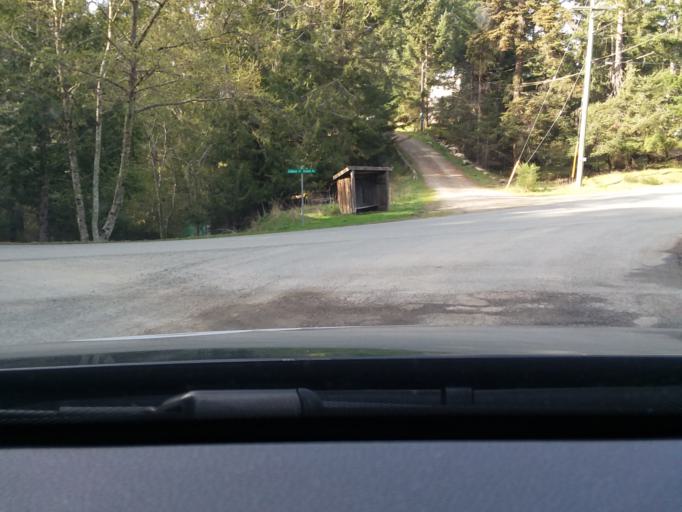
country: CA
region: British Columbia
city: North Saanich
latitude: 48.7714
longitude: -123.2934
